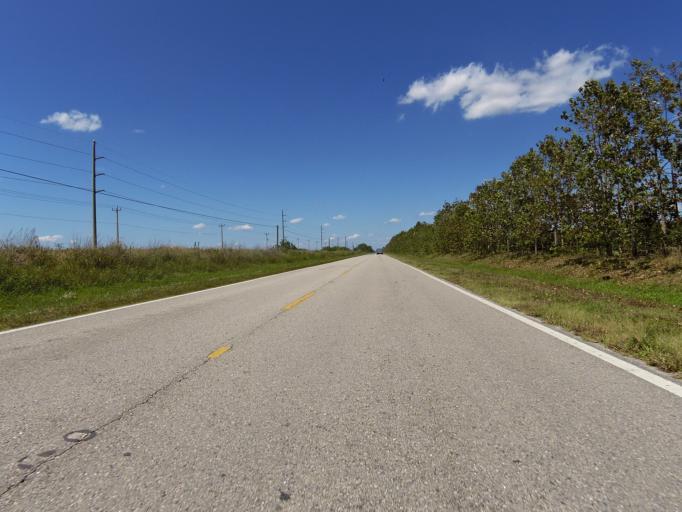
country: US
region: Florida
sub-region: Collier County
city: Immokalee
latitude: 26.3213
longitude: -81.4165
